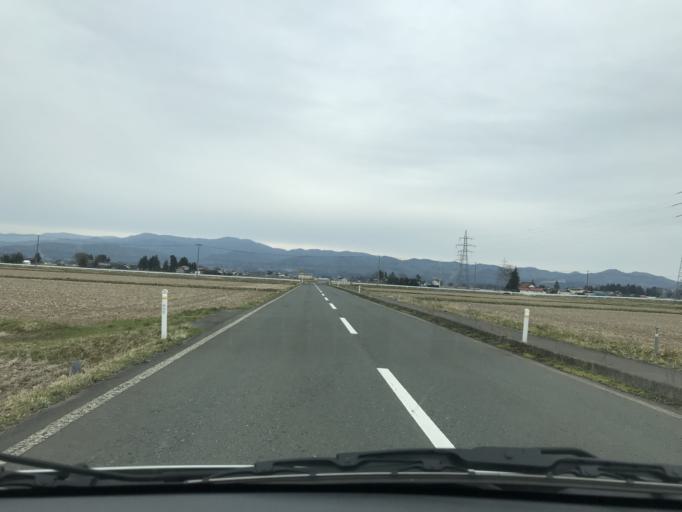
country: JP
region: Iwate
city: Mizusawa
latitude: 39.0858
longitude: 141.1423
